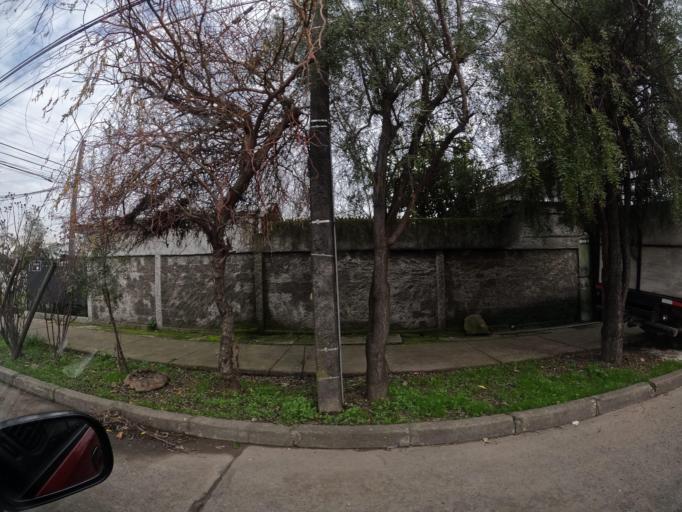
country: CL
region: Maule
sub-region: Provincia de Linares
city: Linares
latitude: -35.8542
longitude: -71.5991
